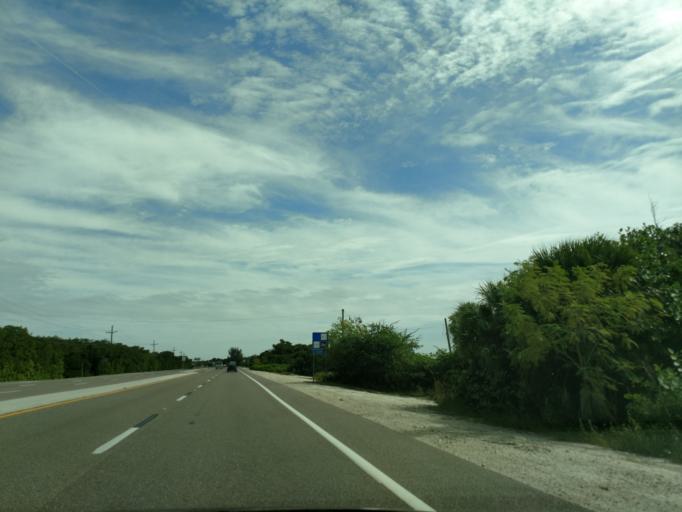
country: US
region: Florida
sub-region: Lee County
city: Punta Rassa
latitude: 26.4852
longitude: -82.0052
